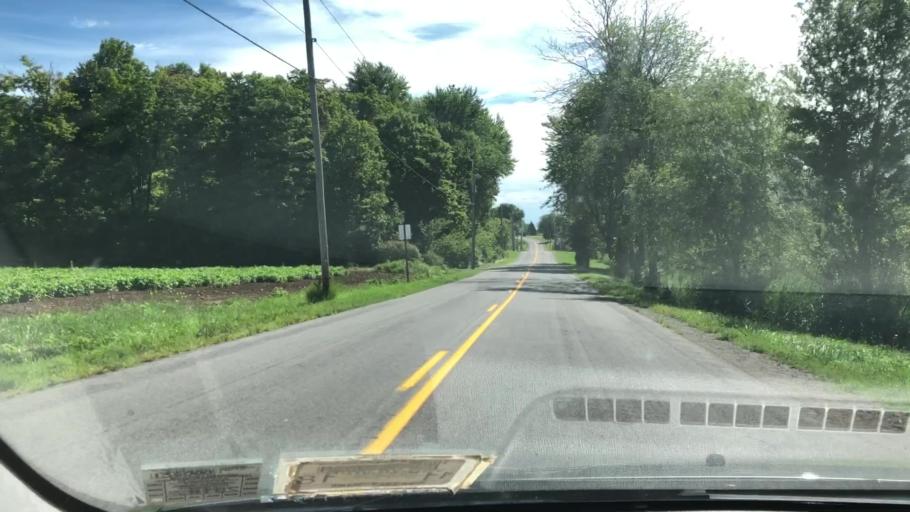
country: US
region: New York
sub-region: Monroe County
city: Fairport
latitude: 43.1283
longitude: -77.3629
